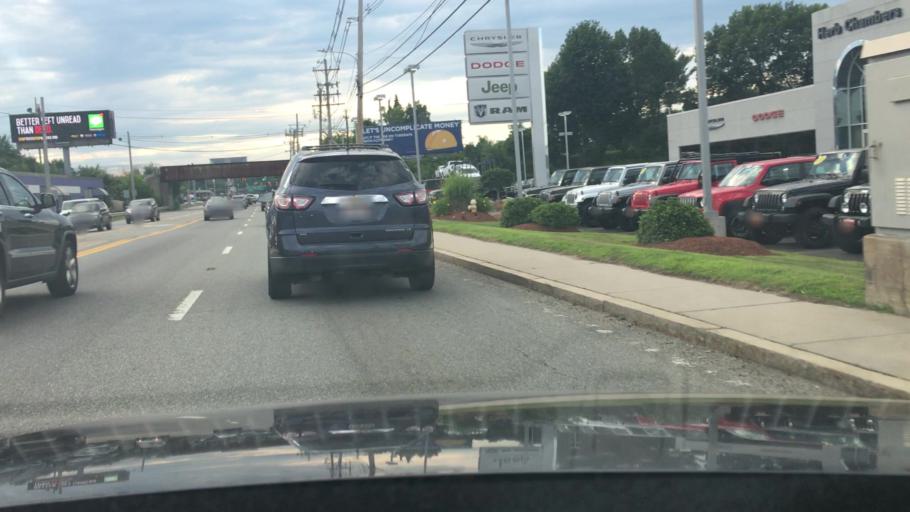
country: US
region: Massachusetts
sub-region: Essex County
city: Danvers
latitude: 42.5556
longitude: -70.9658
